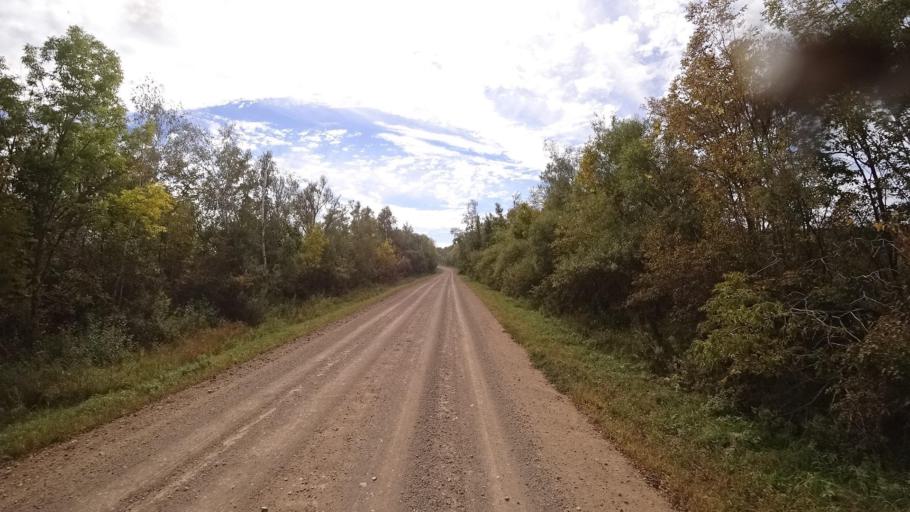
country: RU
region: Primorskiy
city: Yakovlevka
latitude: 44.5284
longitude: 133.5971
